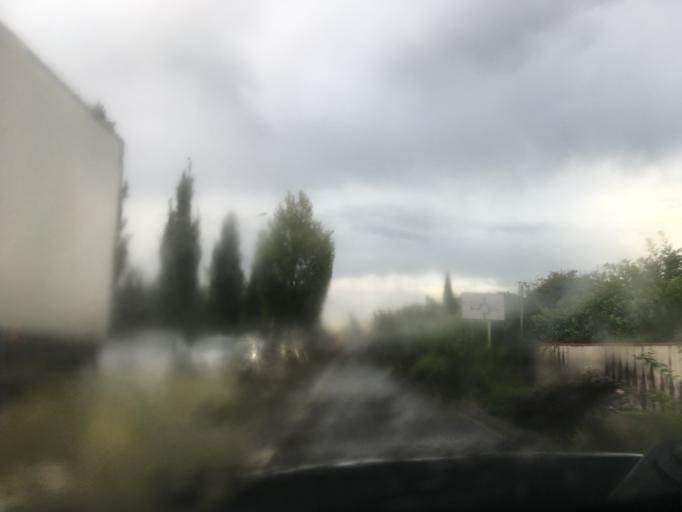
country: FR
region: Midi-Pyrenees
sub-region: Departement de la Haute-Garonne
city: Cugnaux
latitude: 43.5640
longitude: 1.3384
